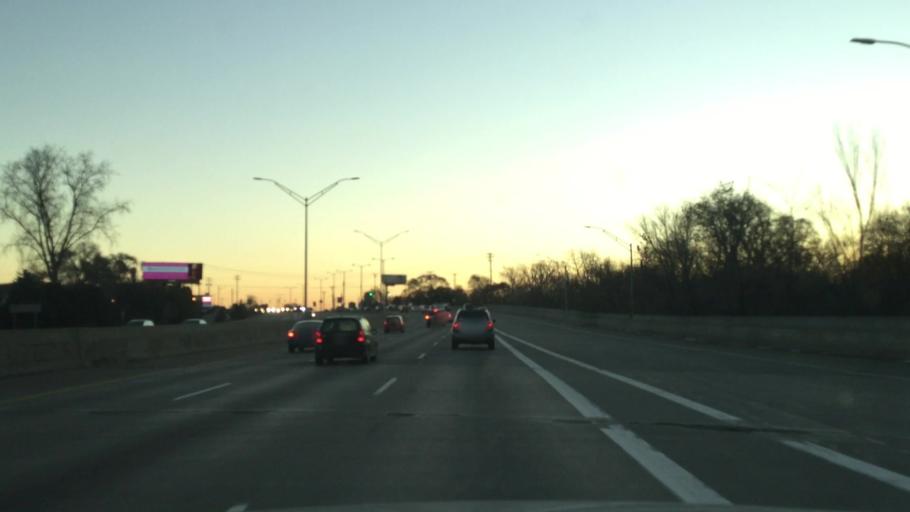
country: US
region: Michigan
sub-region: Macomb County
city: Utica
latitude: 42.6249
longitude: -83.0381
